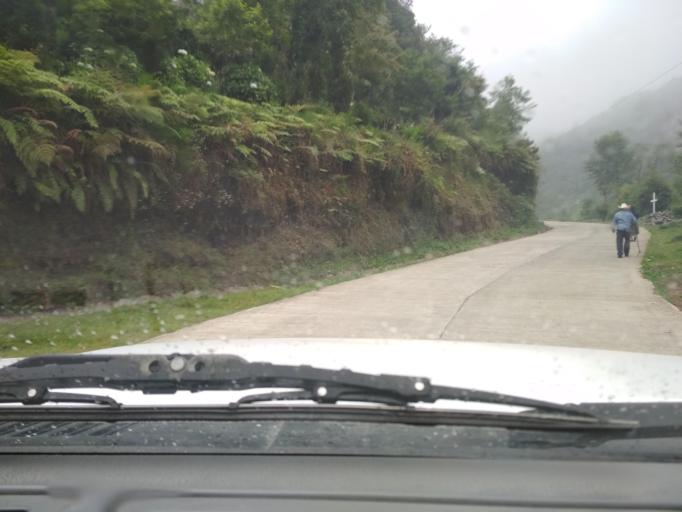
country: MX
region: Veracruz
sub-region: La Perla
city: Barrio de San Miguel
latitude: 18.9557
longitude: -97.1251
